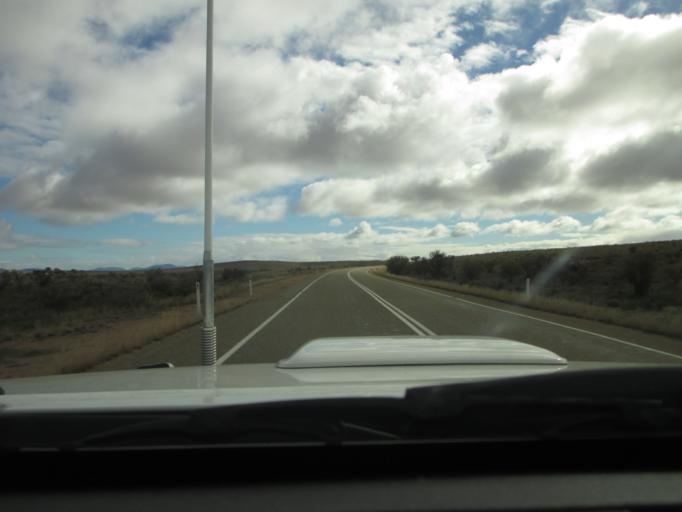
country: AU
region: South Australia
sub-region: Flinders Ranges
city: Quorn
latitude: -32.1071
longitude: 138.5024
